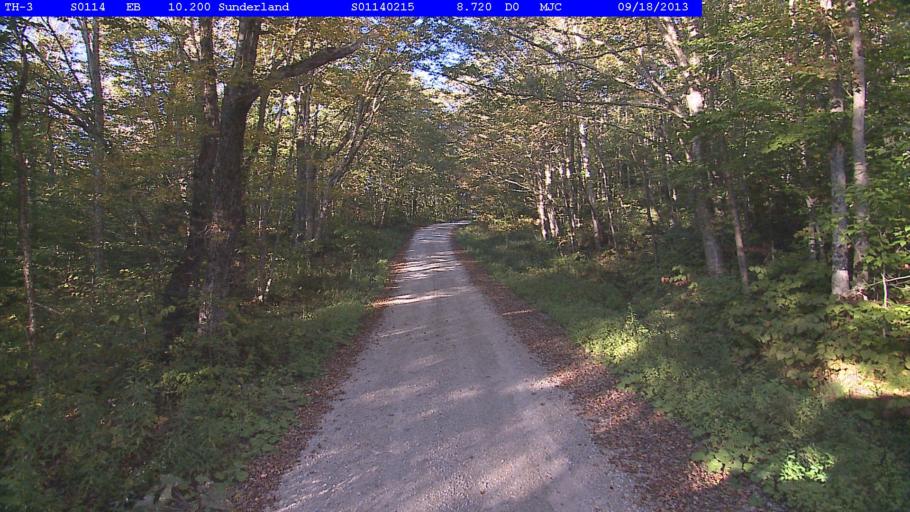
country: US
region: Vermont
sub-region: Bennington County
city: Manchester Center
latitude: 43.0550
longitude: -73.0194
